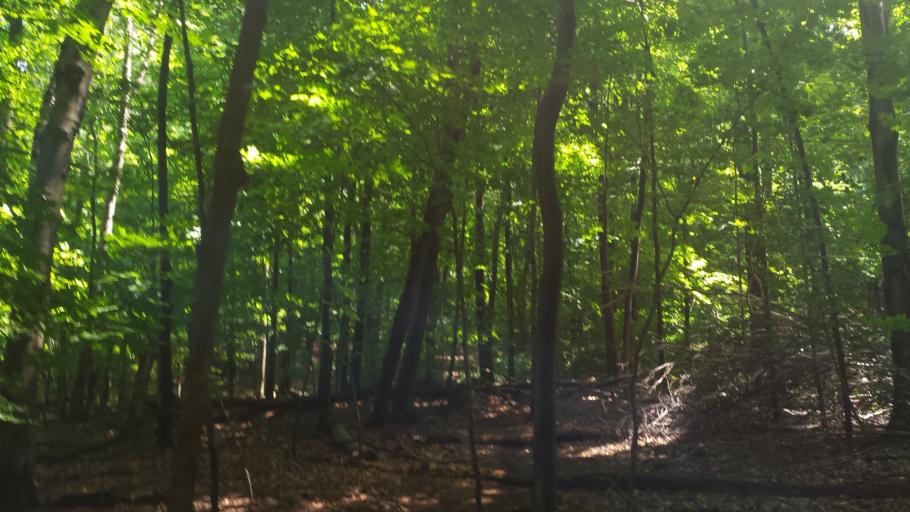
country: US
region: New York
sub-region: Westchester County
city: Hawthorne
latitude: 41.1208
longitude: -73.8018
